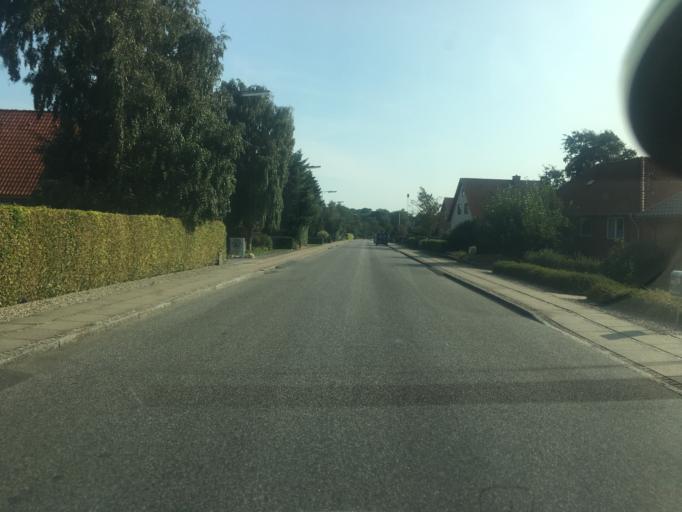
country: DK
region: South Denmark
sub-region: Tonder Kommune
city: Tonder
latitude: 54.9451
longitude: 8.8792
